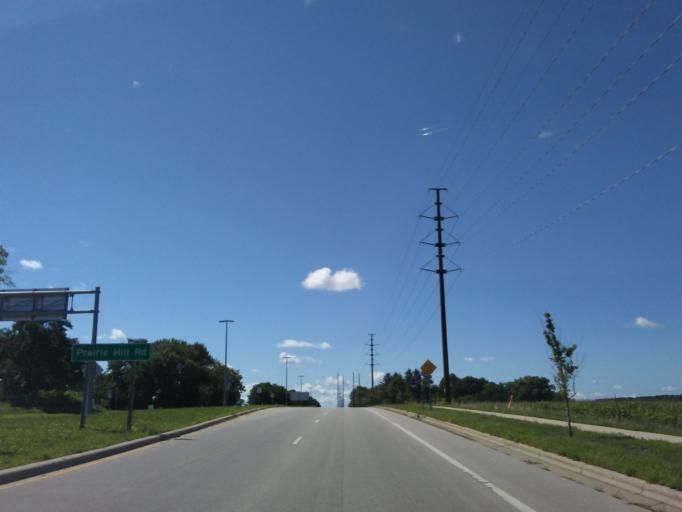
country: US
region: Wisconsin
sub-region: Dane County
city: Verona
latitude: 43.0451
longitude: -89.5329
